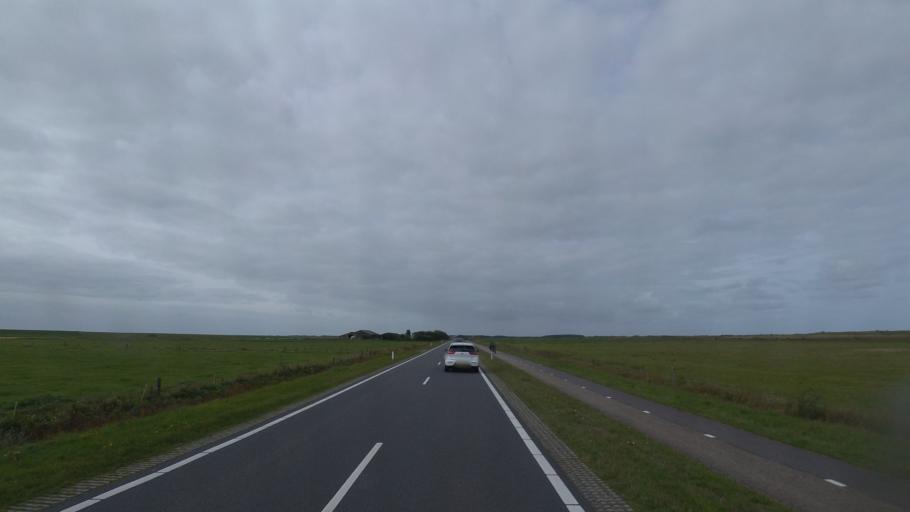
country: NL
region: Friesland
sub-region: Gemeente Ameland
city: Nes
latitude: 53.4458
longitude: 5.7497
